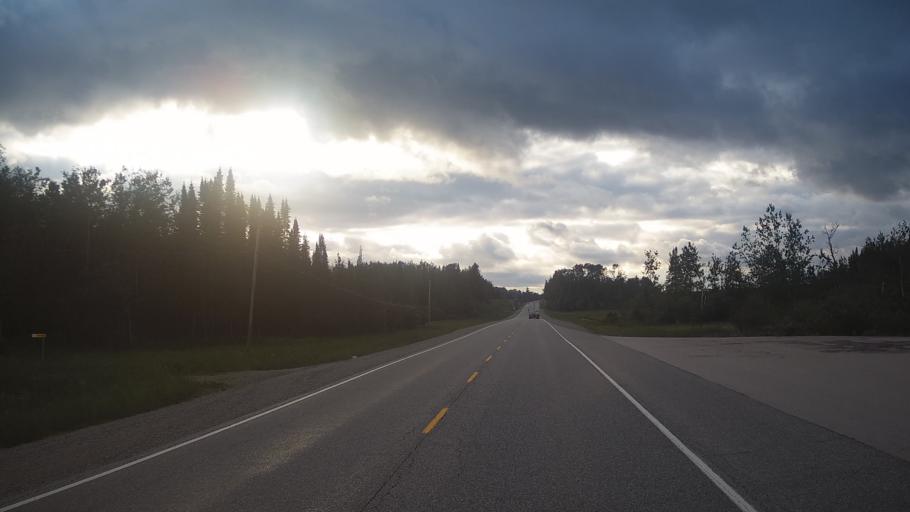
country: CA
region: Ontario
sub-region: Rainy River District
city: Atikokan
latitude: 49.0094
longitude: -90.4206
